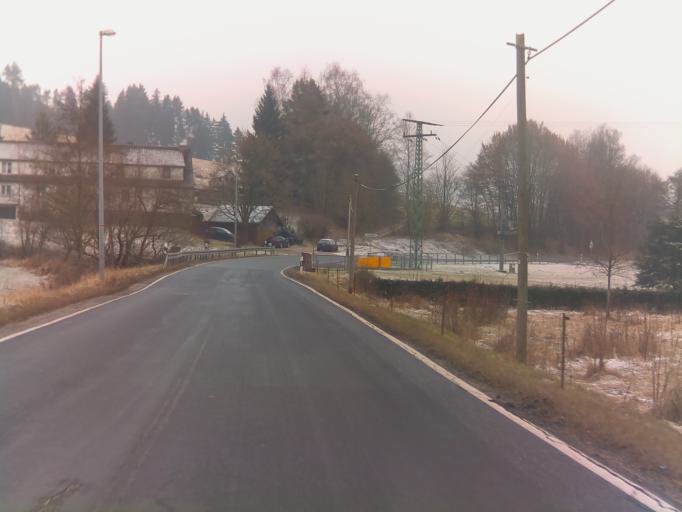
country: DE
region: Thuringia
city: Viernau
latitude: 50.6568
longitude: 10.5586
